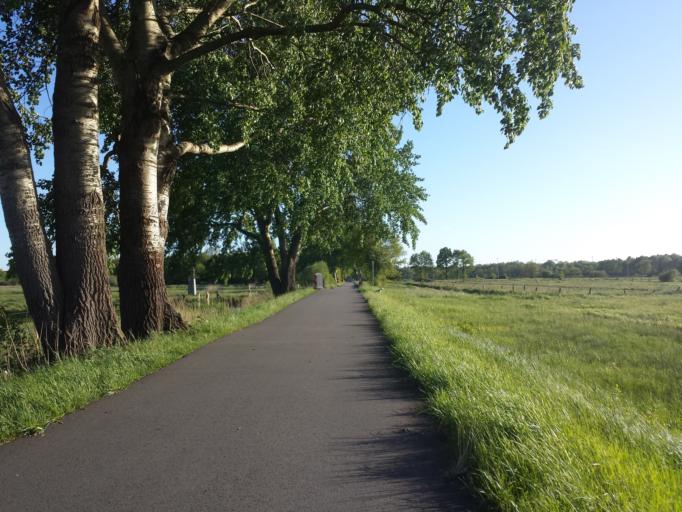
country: DE
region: Lower Saxony
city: Lilienthal
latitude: 53.1175
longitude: 8.8799
